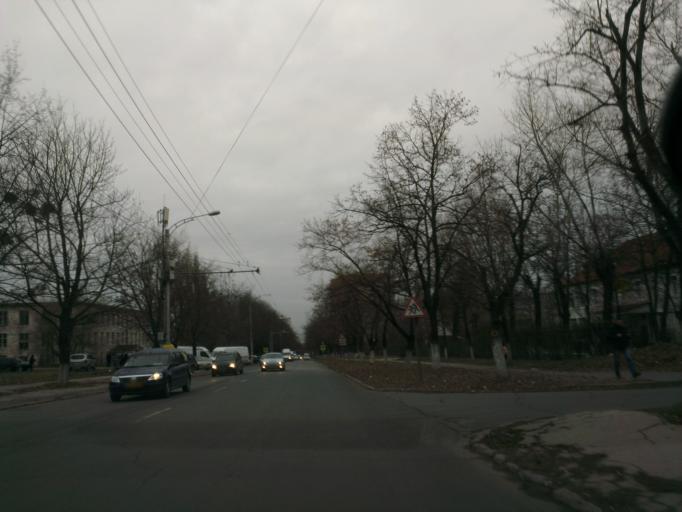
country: MD
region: Chisinau
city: Chisinau
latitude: 46.9899
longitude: 28.8453
